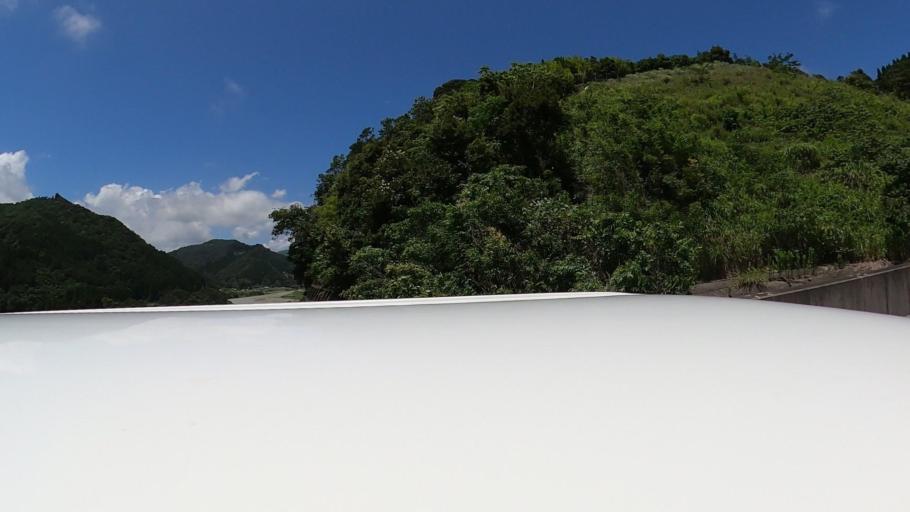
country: JP
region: Miyazaki
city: Takanabe
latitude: 32.3447
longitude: 131.6000
